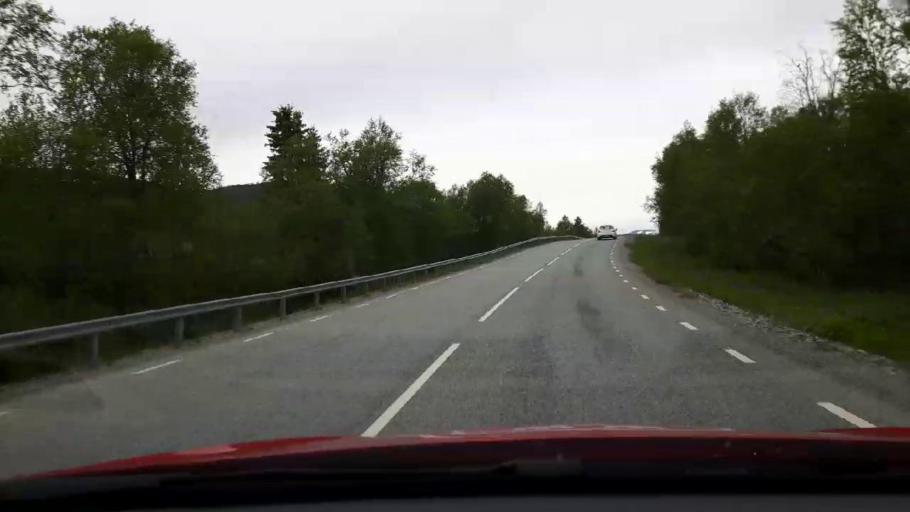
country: NO
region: Sor-Trondelag
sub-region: Tydal
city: Aas
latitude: 62.6778
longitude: 12.4205
